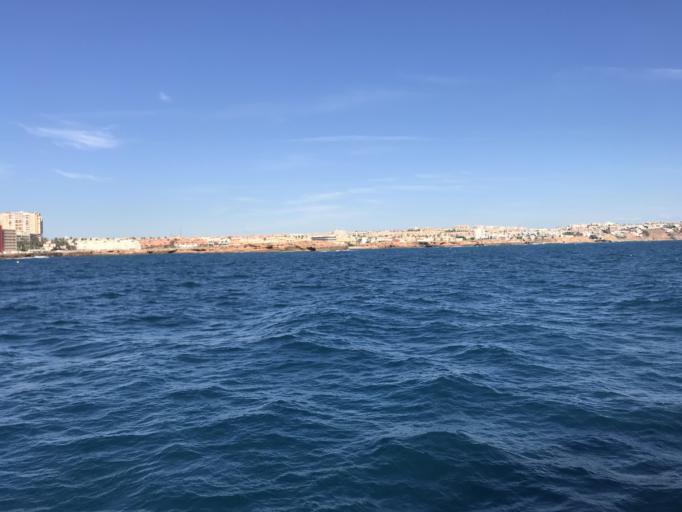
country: ES
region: Valencia
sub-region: Provincia de Alicante
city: Torrevieja
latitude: 37.9819
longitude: -0.6519
